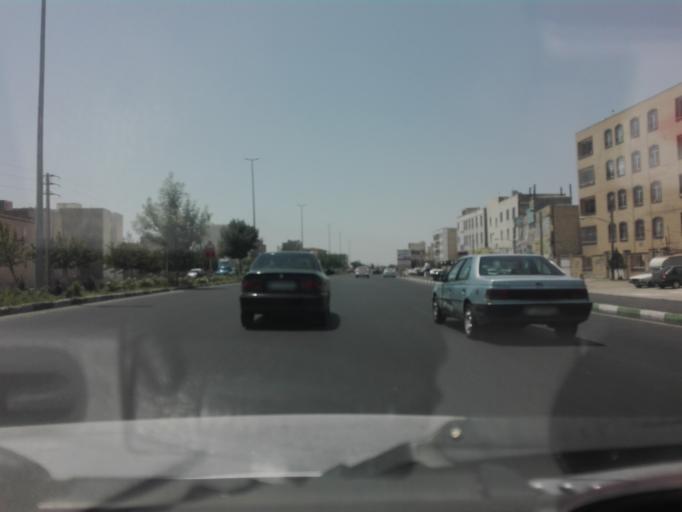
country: IR
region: Tehran
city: Malard
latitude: 35.7105
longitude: 50.9810
